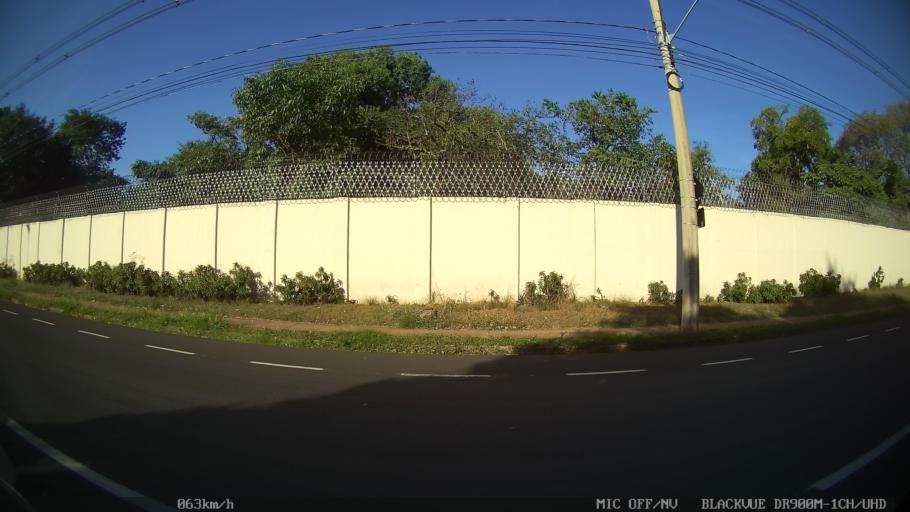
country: BR
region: Sao Paulo
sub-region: Sao Jose Do Rio Preto
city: Sao Jose do Rio Preto
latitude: -20.8471
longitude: -49.4118
